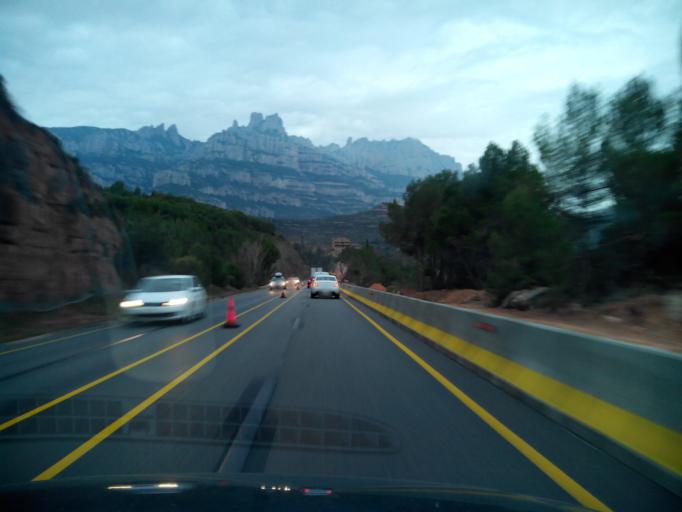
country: ES
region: Catalonia
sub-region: Provincia de Barcelona
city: Monistrol de Montserrat
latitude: 41.6024
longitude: 1.8802
